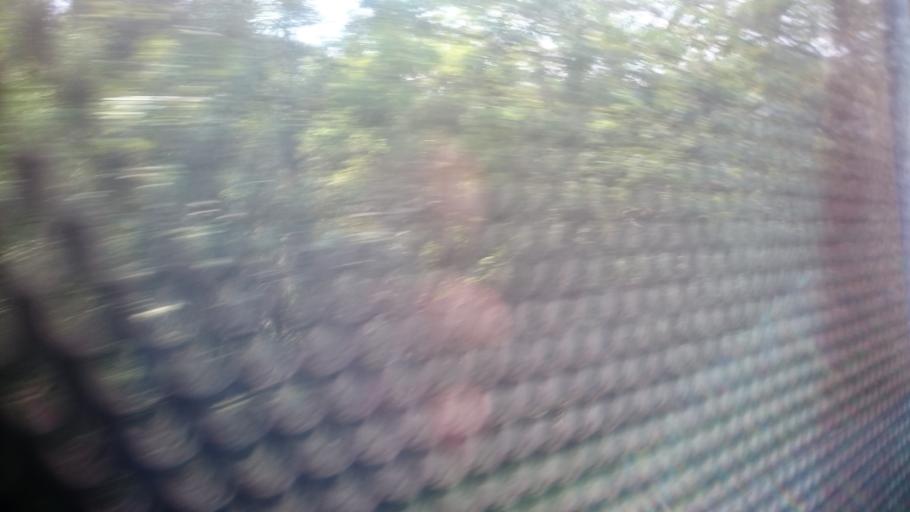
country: ES
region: Asturias
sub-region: Province of Asturias
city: Amieva
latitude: 43.3013
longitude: -5.0370
